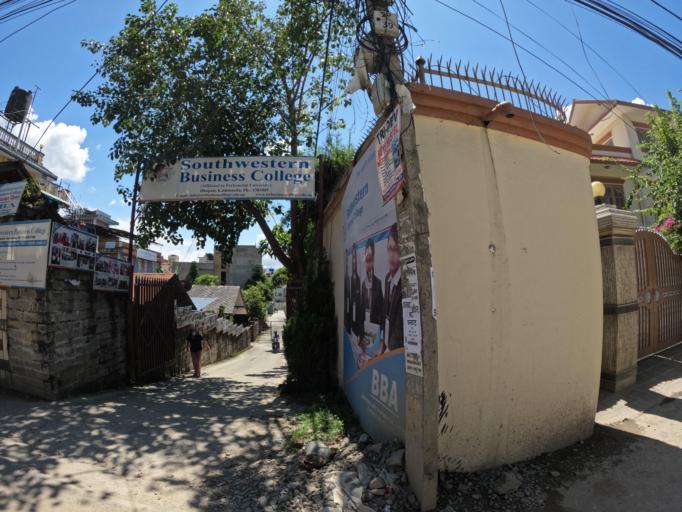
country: NP
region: Central Region
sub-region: Bagmati Zone
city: Kathmandu
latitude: 27.7401
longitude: 85.3231
